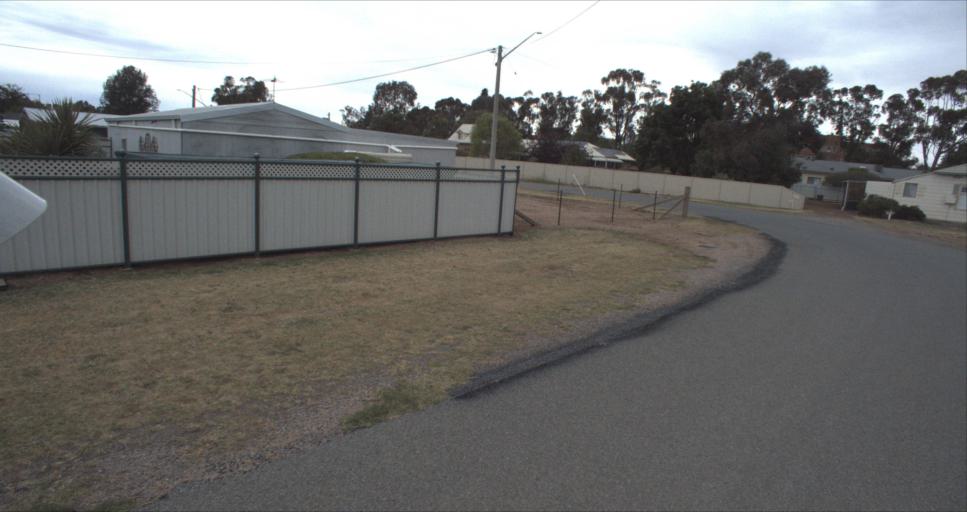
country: AU
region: New South Wales
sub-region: Leeton
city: Leeton
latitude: -34.5430
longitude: 146.4083
